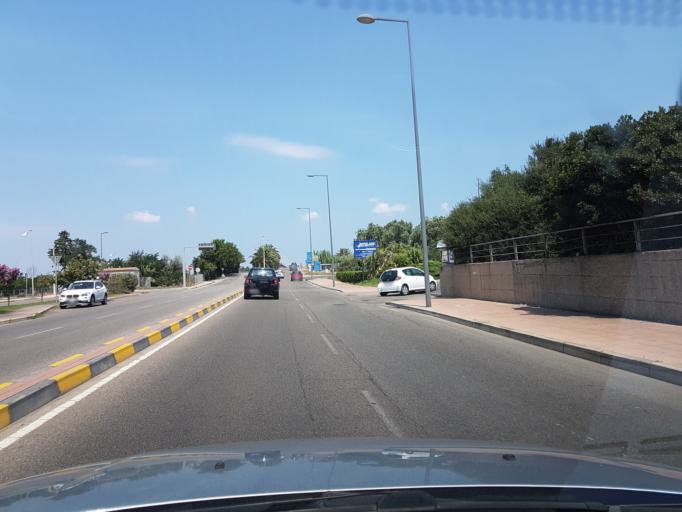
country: IT
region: Sardinia
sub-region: Provincia di Oristano
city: Oristano
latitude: 39.9156
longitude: 8.5852
